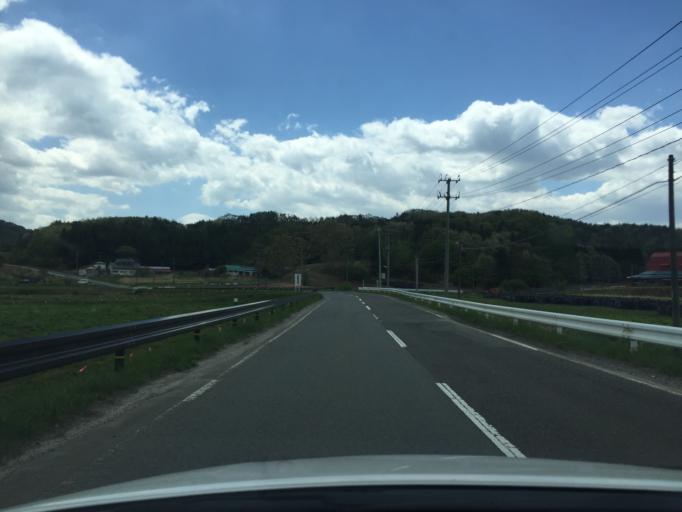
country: JP
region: Fukushima
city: Yanagawamachi-saiwaicho
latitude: 37.7155
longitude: 140.6909
